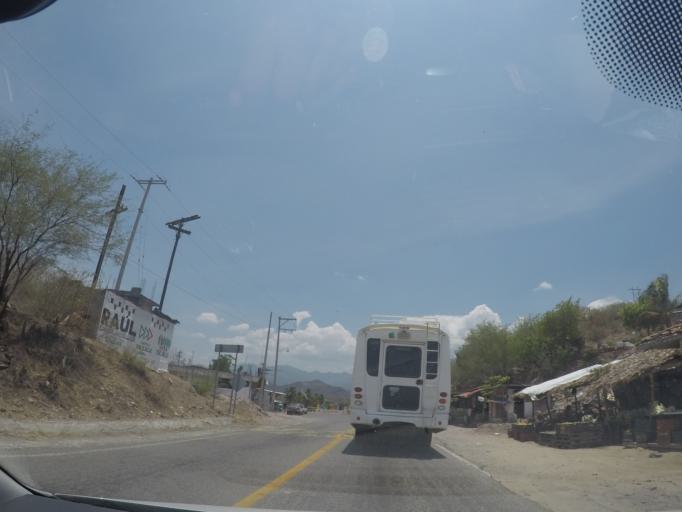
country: MX
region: Oaxaca
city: Magdalena Tequisistlan
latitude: 16.4128
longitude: -95.5948
